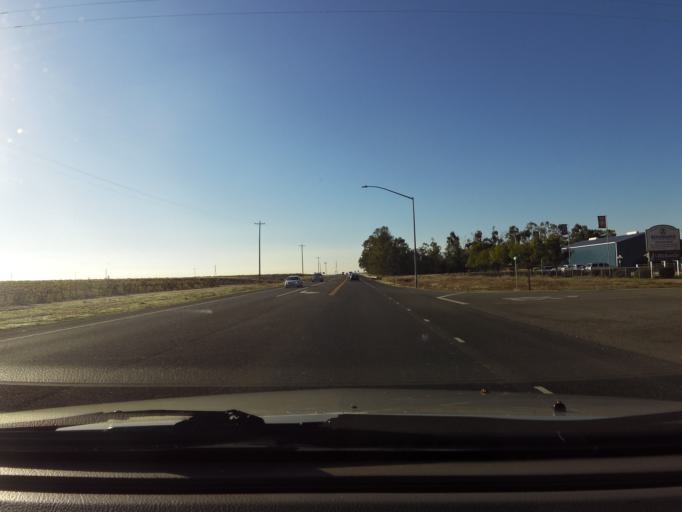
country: US
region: California
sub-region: Madera County
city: Bonadelle Ranchos-Madera Ranchos
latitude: 36.9560
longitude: -119.7942
